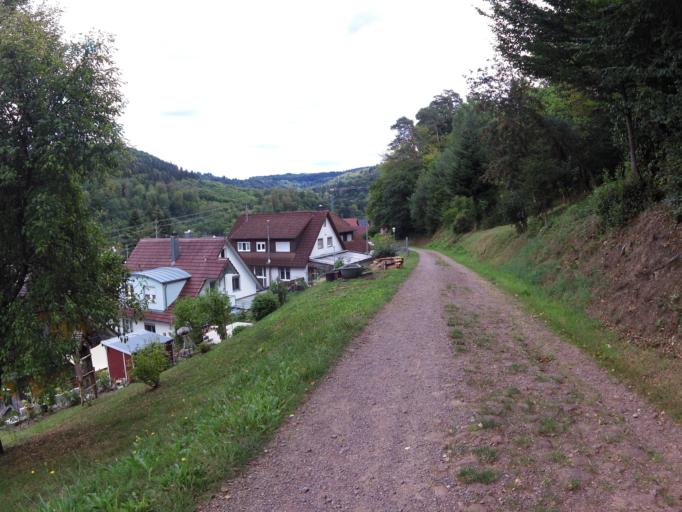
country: DE
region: Baden-Wuerttemberg
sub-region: Freiburg Region
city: Lahr
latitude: 48.3067
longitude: 7.8603
